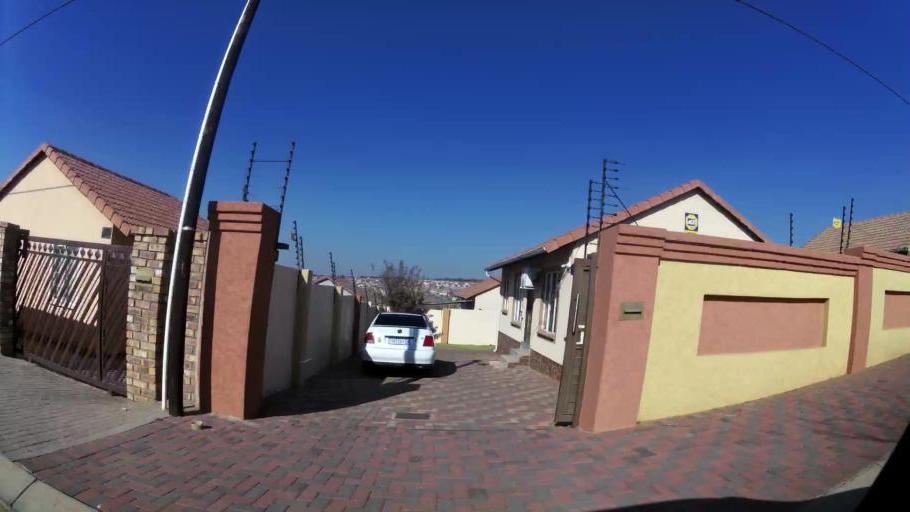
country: ZA
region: Gauteng
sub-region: West Rand District Municipality
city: Muldersdriseloop
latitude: -26.0333
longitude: 27.9148
